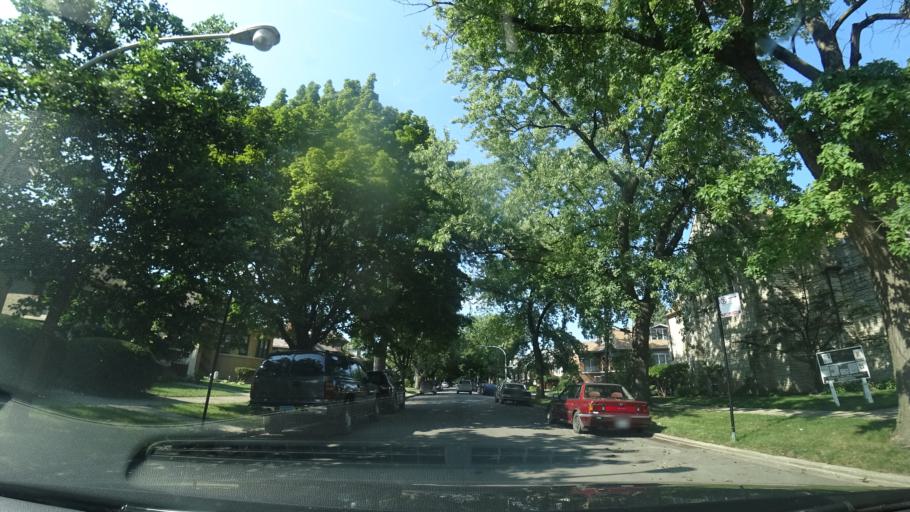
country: US
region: Illinois
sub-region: Cook County
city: Lincolnwood
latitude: 41.9699
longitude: -87.7379
